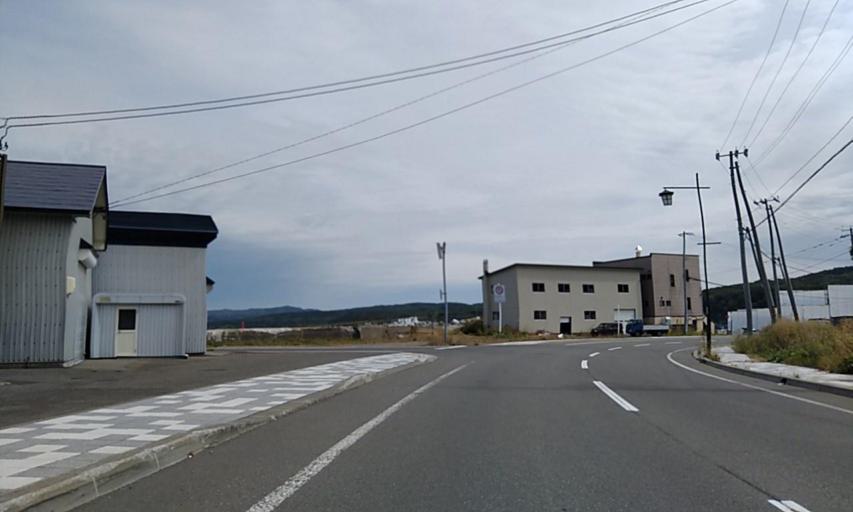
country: JP
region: Hokkaido
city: Rumoi
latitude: 43.8576
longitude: 141.5273
